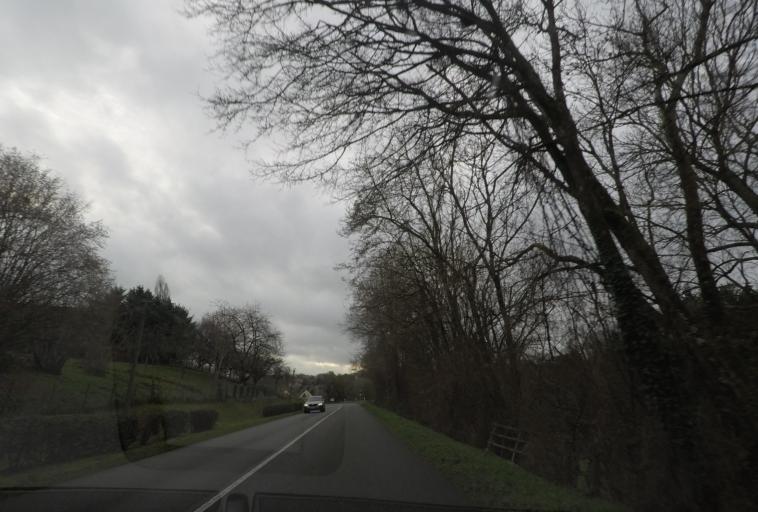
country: FR
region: Pays de la Loire
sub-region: Departement de la Sarthe
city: Vibraye
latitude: 47.9965
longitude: 0.7630
